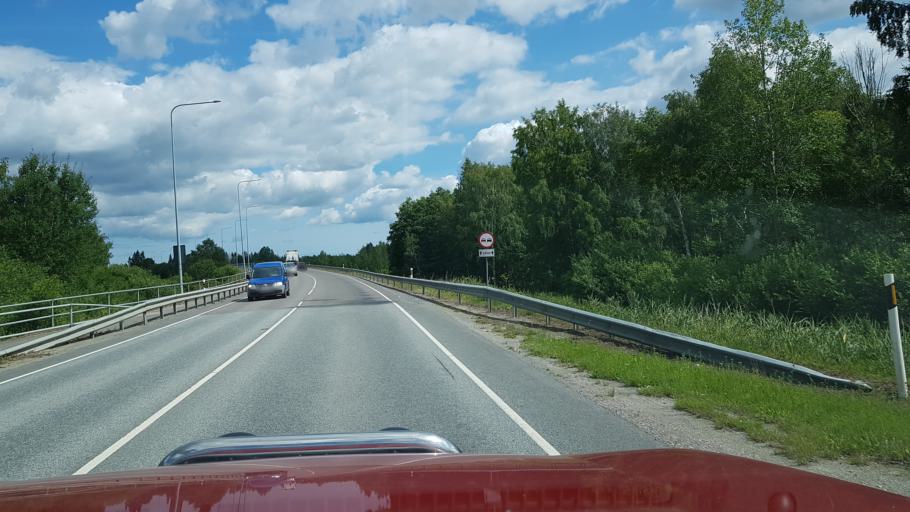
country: EE
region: Laeaene-Virumaa
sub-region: Someru vald
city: Someru
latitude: 59.3563
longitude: 26.4012
